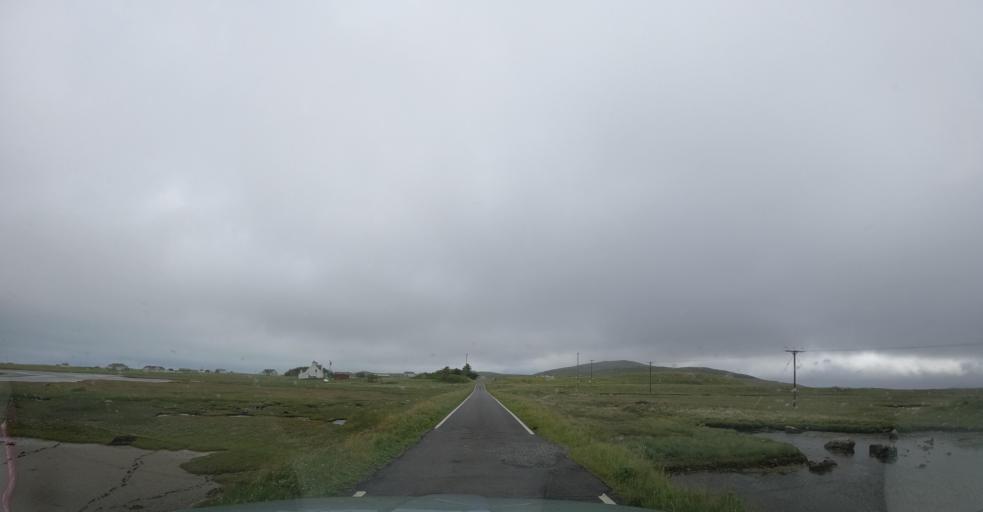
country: GB
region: Scotland
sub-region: Eilean Siar
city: Isle of North Uist
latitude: 57.6537
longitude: -7.2458
